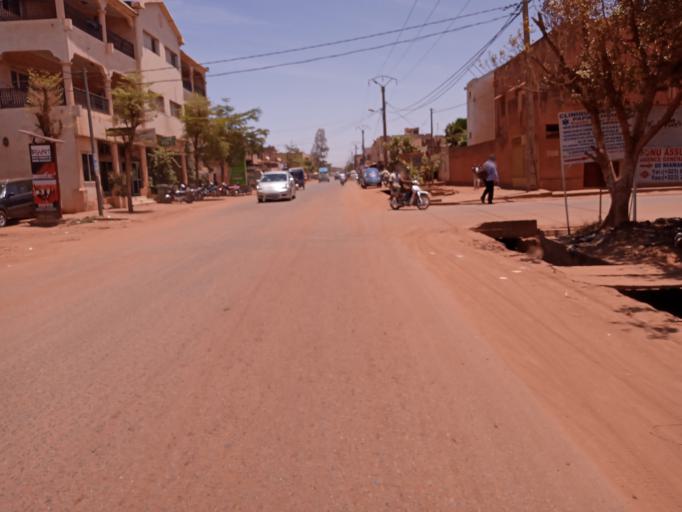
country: ML
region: Bamako
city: Bamako
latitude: 12.5883
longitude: -7.9766
